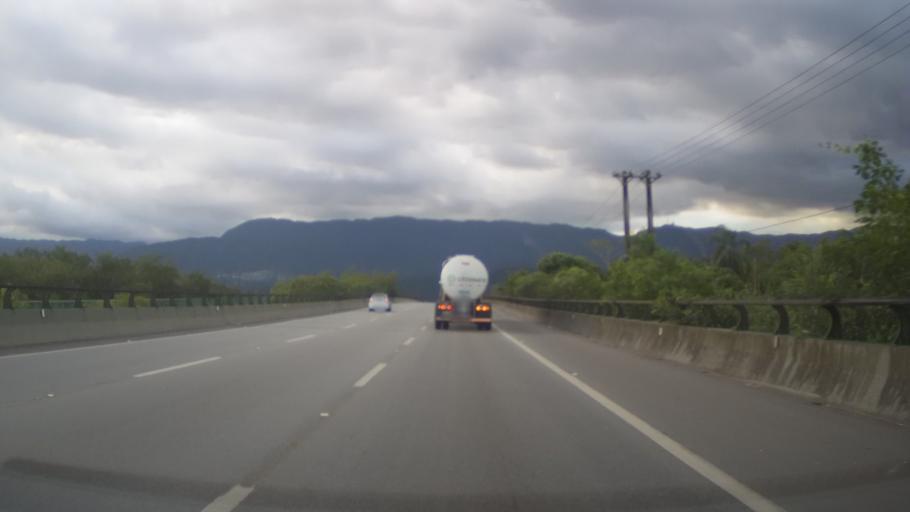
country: BR
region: Sao Paulo
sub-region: Cubatao
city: Cubatao
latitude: -23.9196
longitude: -46.4361
